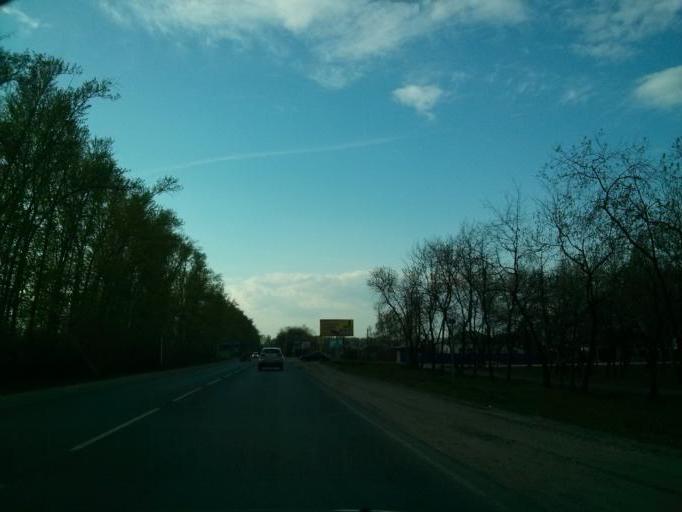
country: RU
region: Vladimir
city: Murom
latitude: 55.5997
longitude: 42.0317
